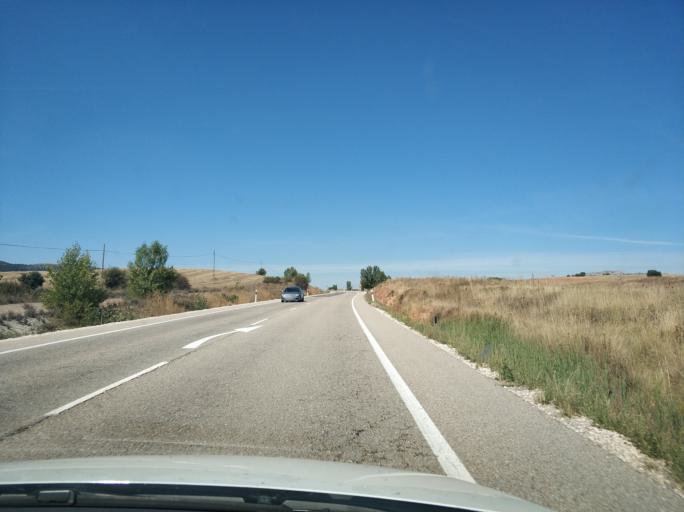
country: ES
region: Castille and Leon
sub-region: Provincia de Burgos
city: Mambrillas de Lara
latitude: 42.0813
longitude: -3.4452
